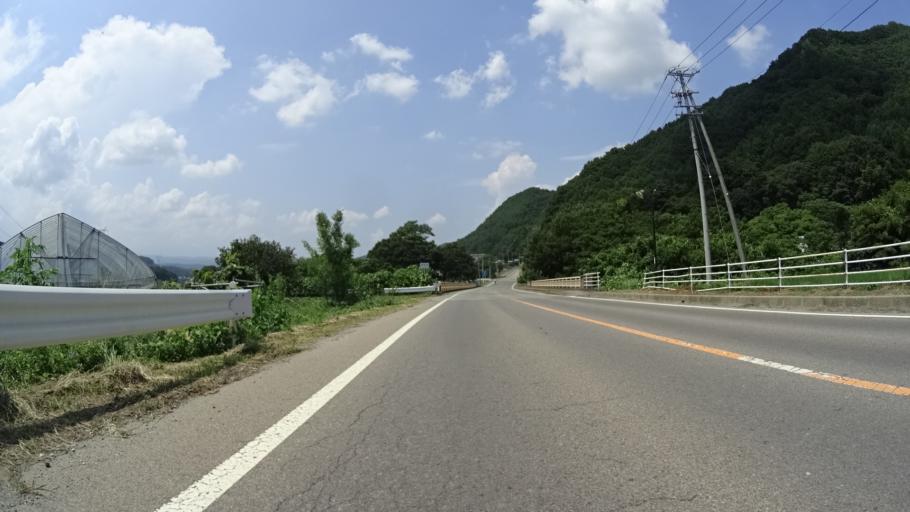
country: JP
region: Nagano
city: Saku
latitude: 36.1443
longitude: 138.5176
